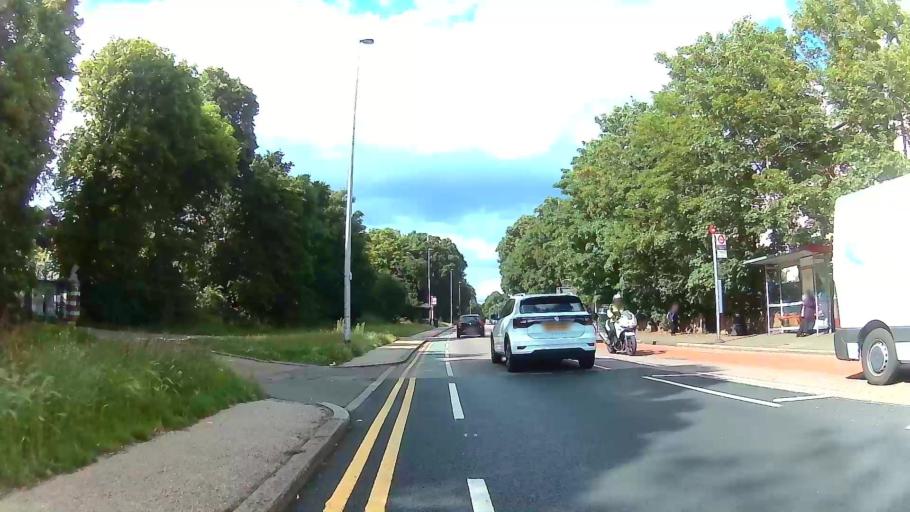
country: GB
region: England
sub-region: Greater London
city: Woodford Green
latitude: 51.5838
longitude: 0.0203
